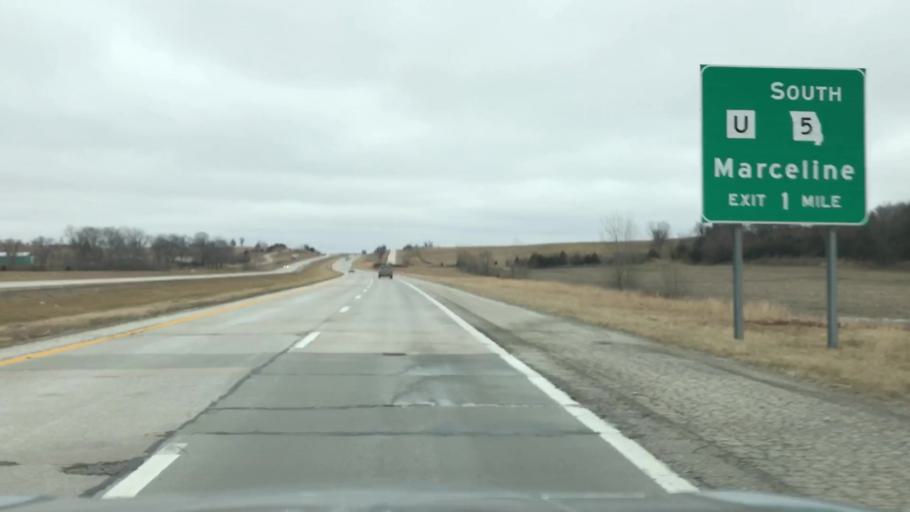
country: US
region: Missouri
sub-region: Linn County
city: Marceline
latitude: 39.7609
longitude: -92.9653
